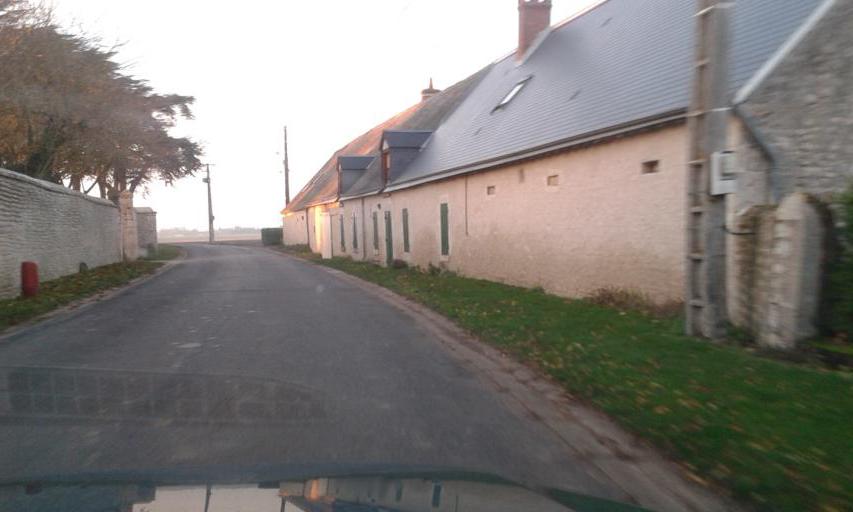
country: FR
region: Centre
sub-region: Departement du Loiret
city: Tavers
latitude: 47.7775
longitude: 1.5459
